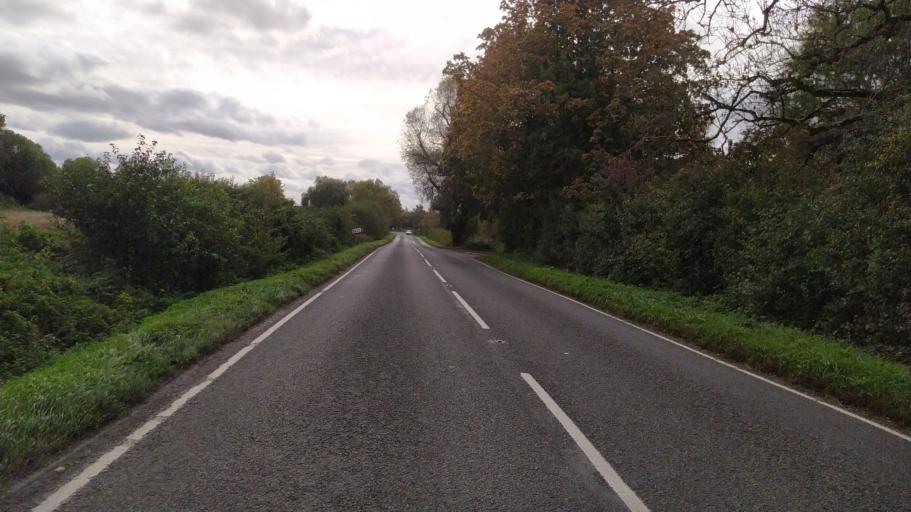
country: GB
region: England
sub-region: Hampshire
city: Romsey
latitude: 51.0411
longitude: -1.5226
